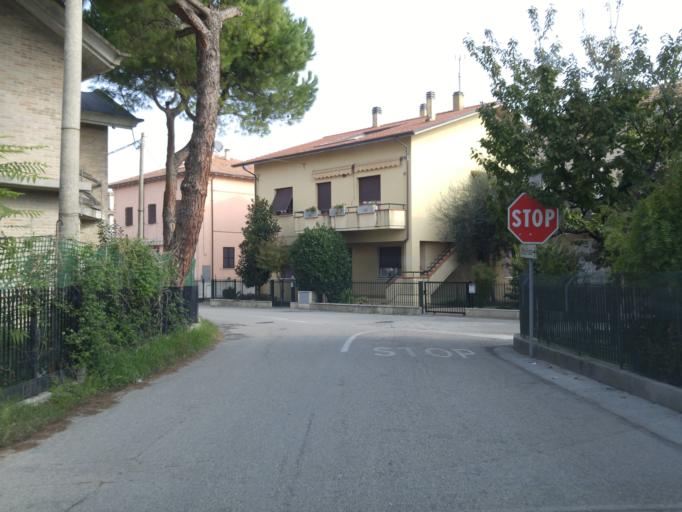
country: IT
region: The Marches
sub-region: Provincia di Pesaro e Urbino
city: Fano
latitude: 43.8284
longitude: 13.0107
